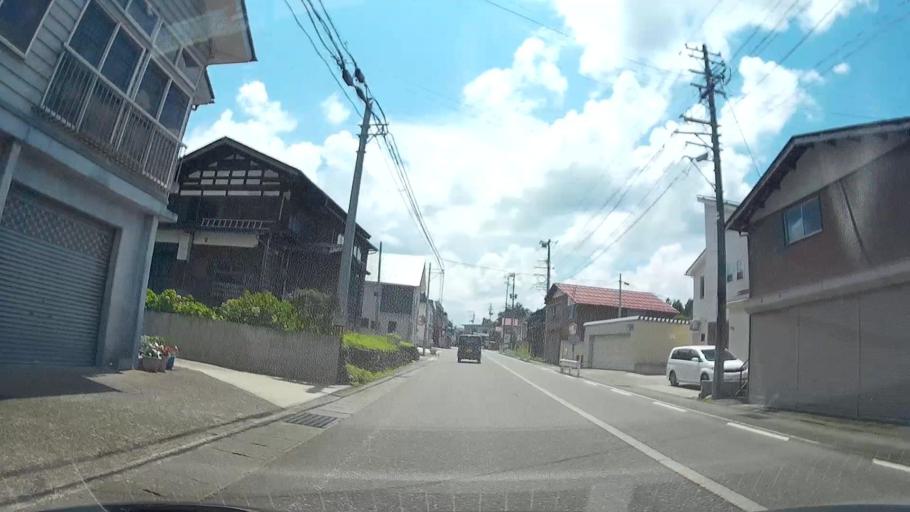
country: JP
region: Niigata
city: Tokamachi
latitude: 37.0776
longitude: 138.7179
